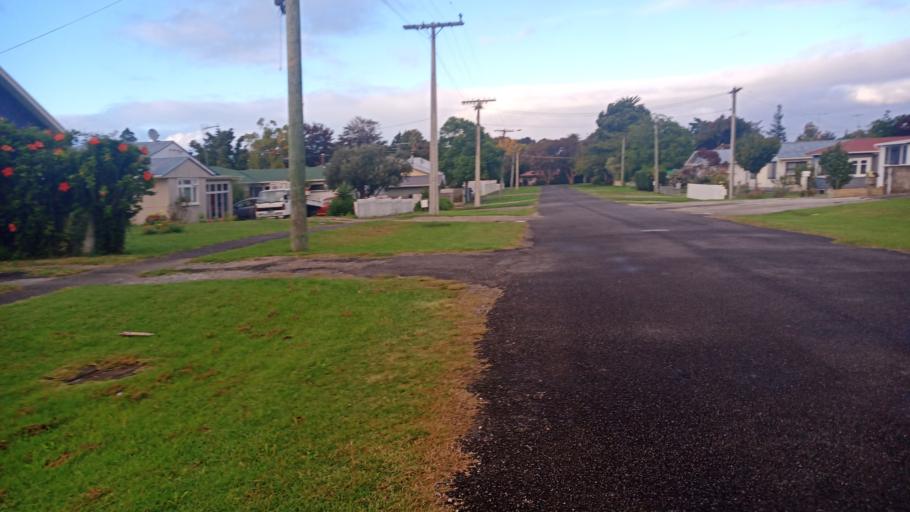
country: NZ
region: Gisborne
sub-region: Gisborne District
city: Gisborne
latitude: -38.6502
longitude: 178.0163
